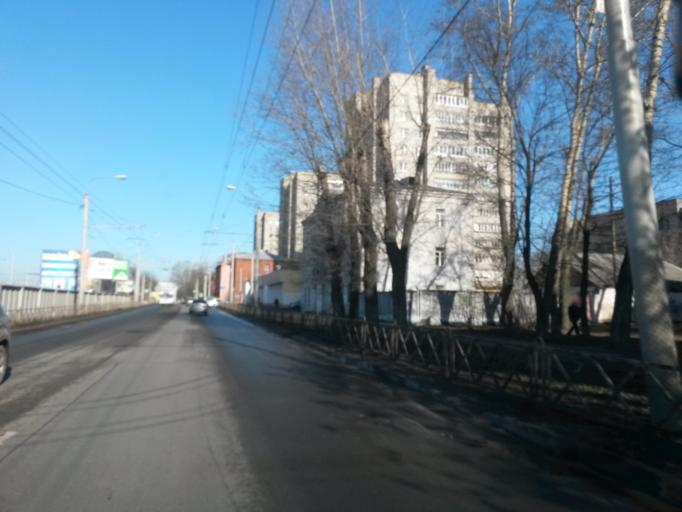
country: RU
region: Jaroslavl
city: Yaroslavl
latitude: 57.6237
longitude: 39.8418
